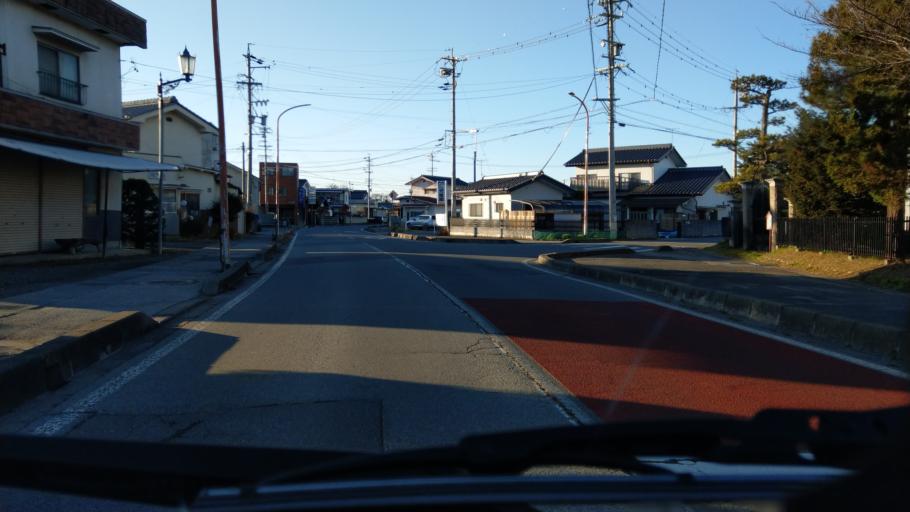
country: JP
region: Nagano
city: Saku
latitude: 36.2371
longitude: 138.4722
